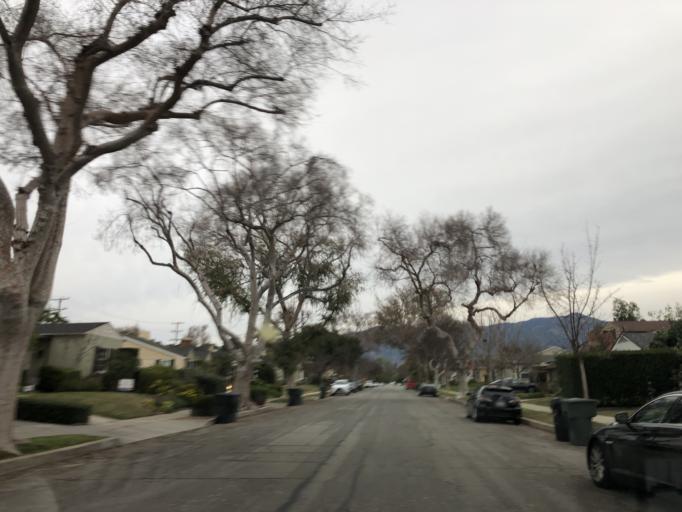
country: US
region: California
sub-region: Los Angeles County
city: San Gabriel
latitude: 34.1081
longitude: -118.1009
